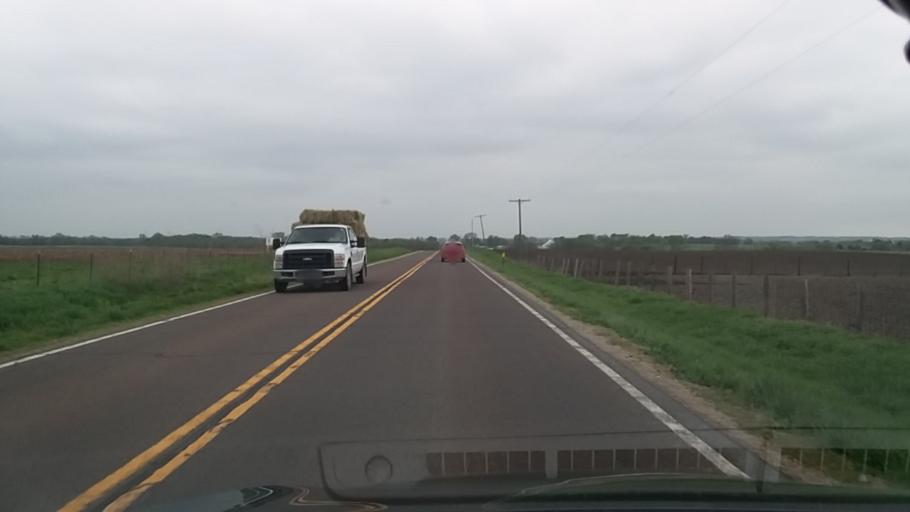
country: US
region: Kansas
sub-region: Douglas County
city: Eudora
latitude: 38.8975
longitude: -95.0934
